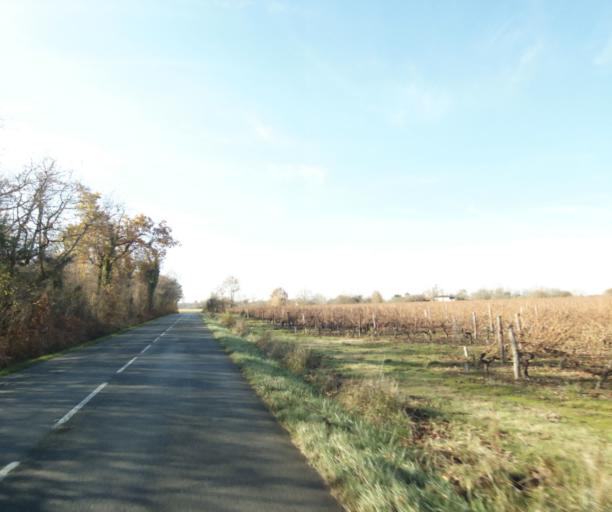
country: FR
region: Poitou-Charentes
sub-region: Departement de la Charente-Maritime
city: Ecoyeux
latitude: 45.7652
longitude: -0.5185
